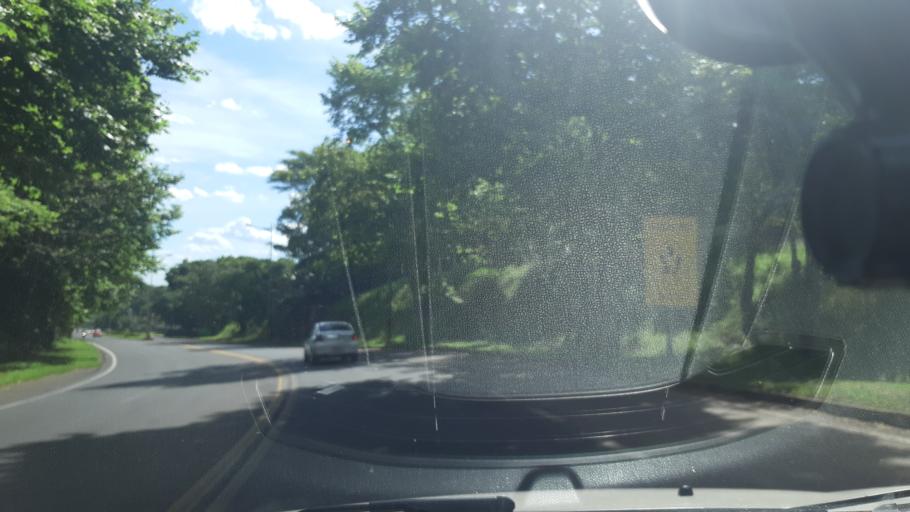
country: BR
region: Rio Grande do Sul
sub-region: Ivoti
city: Ivoti
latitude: -29.6235
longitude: -51.1337
